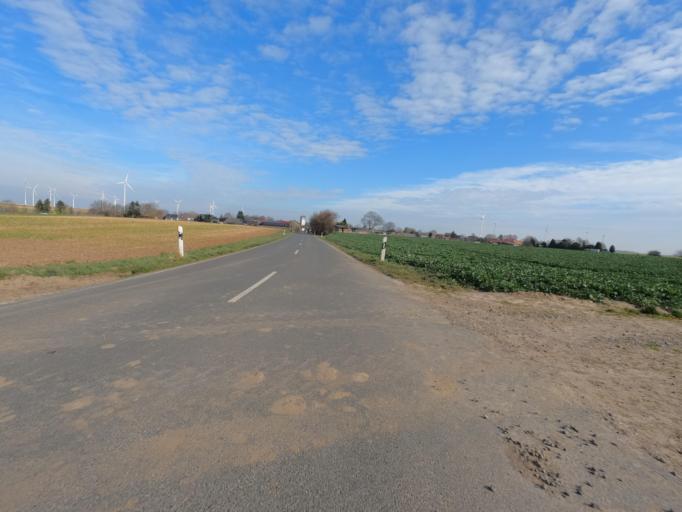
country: DE
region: North Rhine-Westphalia
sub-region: Regierungsbezirk Koln
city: Linnich
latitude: 50.9969
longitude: 6.3175
